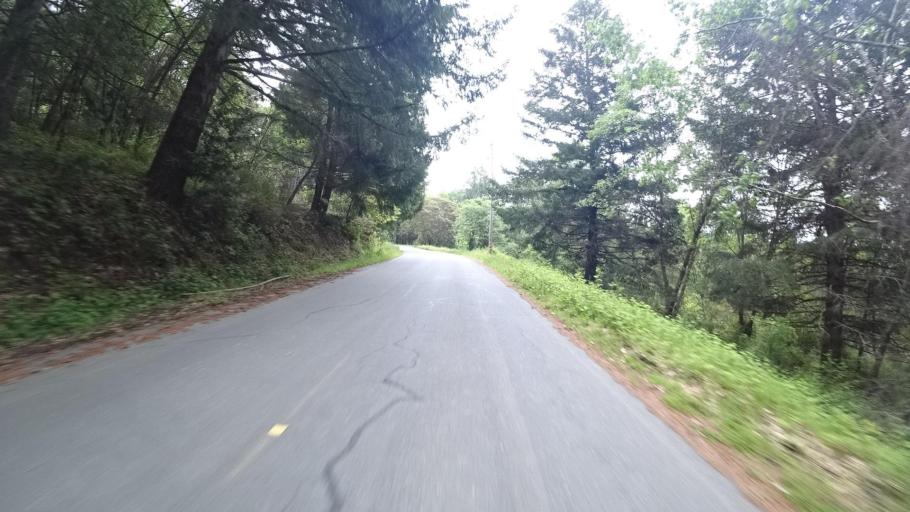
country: US
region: California
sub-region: Humboldt County
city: Willow Creek
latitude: 41.1085
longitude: -123.7124
